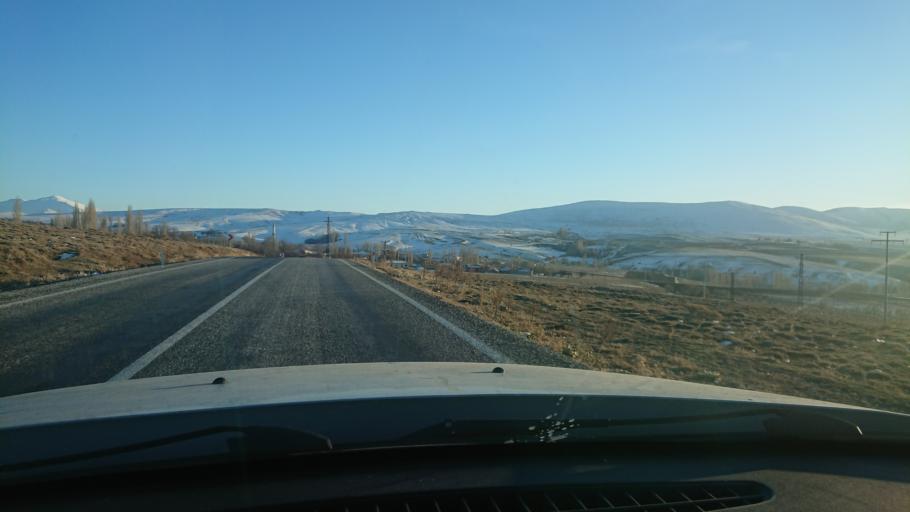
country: TR
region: Aksaray
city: Ortakoy
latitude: 38.7605
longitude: 33.9331
